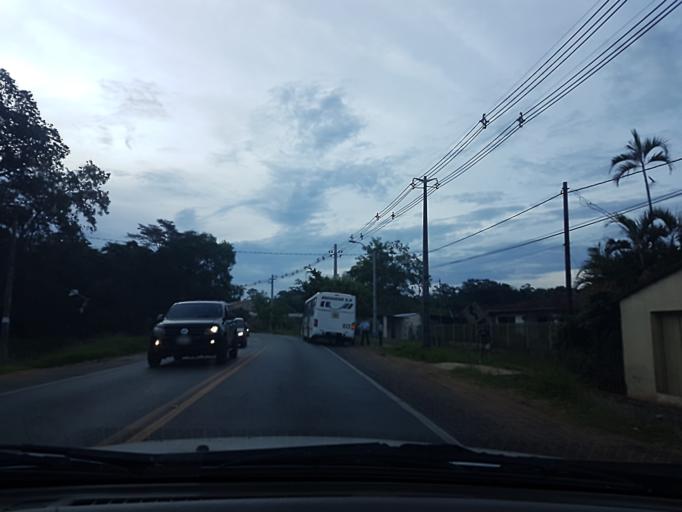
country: PY
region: Central
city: San Lorenzo
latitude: -25.2844
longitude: -57.4644
